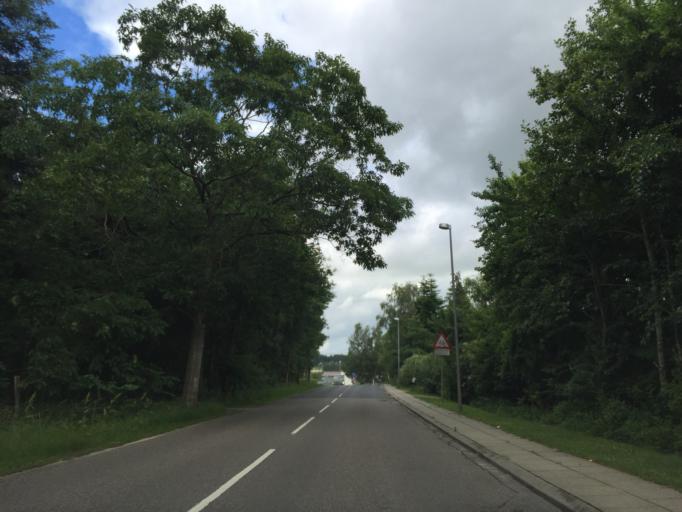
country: DK
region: Central Jutland
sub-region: Silkeborg Kommune
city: Svejbaek
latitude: 56.1797
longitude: 9.6446
